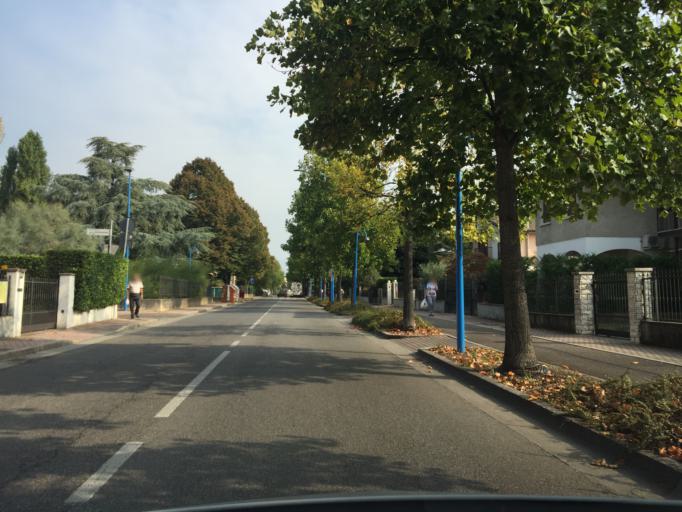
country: IT
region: Lombardy
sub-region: Provincia di Brescia
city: Folzano
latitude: 45.5090
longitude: 10.1863
